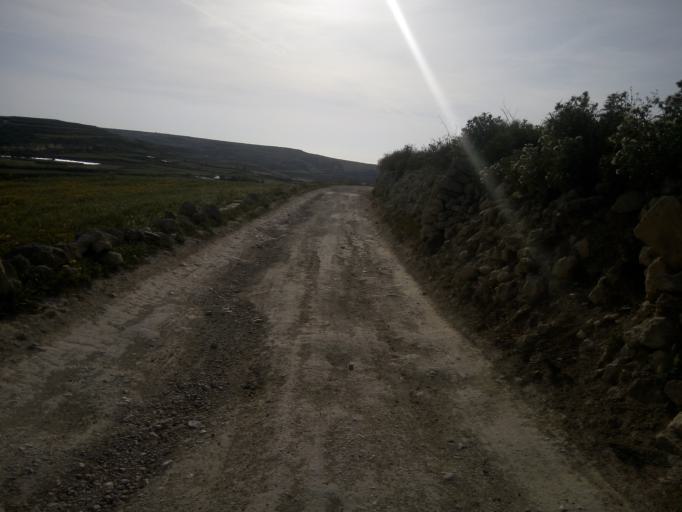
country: MT
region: Saint Lucia
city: Saint Lucia
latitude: 36.0451
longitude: 14.2102
